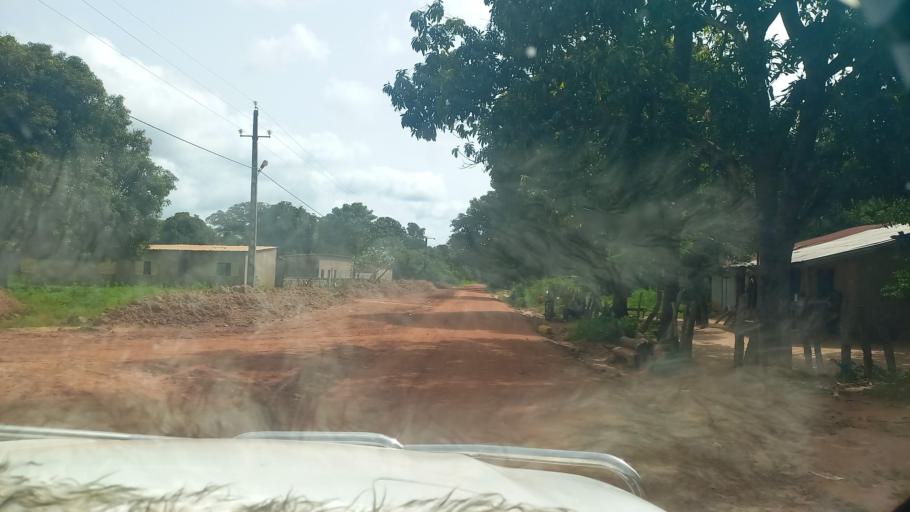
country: SN
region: Ziguinchor
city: Bignona
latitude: 12.7509
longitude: -16.2811
